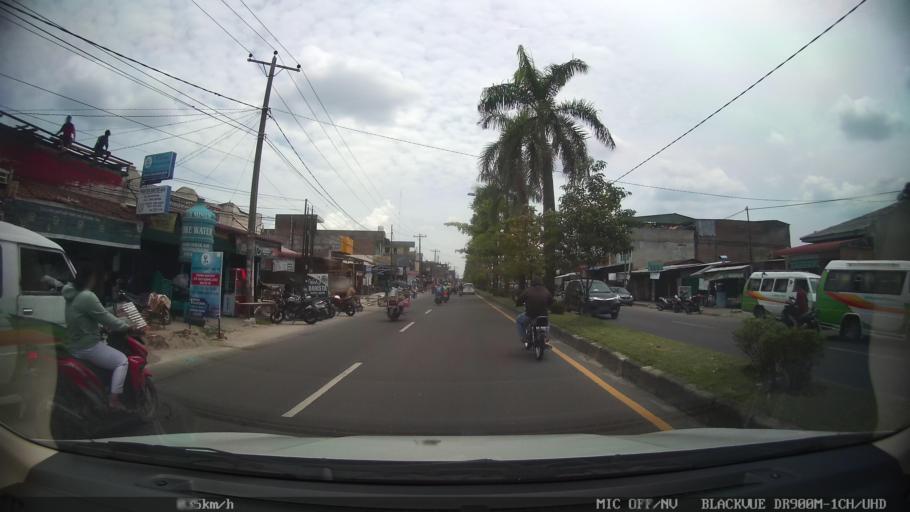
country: ID
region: North Sumatra
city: Deli Tua
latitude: 3.5365
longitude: 98.6504
